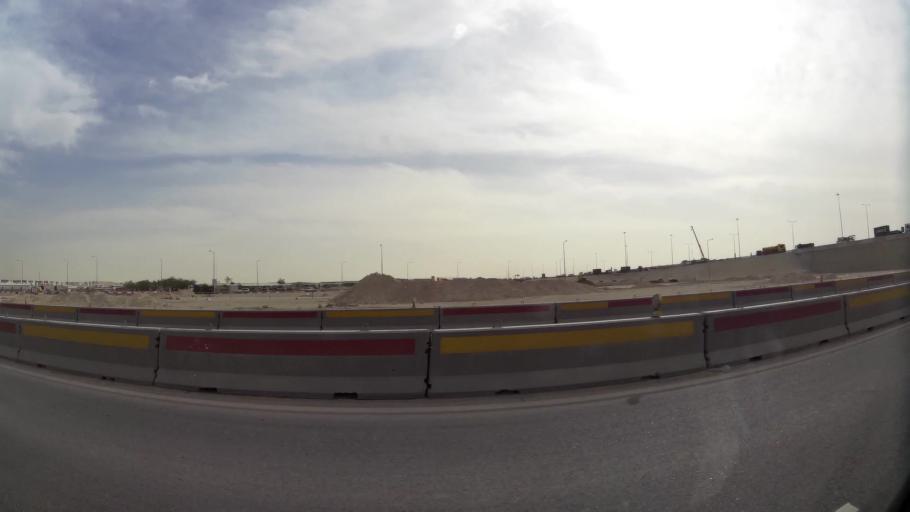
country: QA
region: Baladiyat ar Rayyan
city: Ar Rayyan
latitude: 25.3298
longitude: 51.3345
